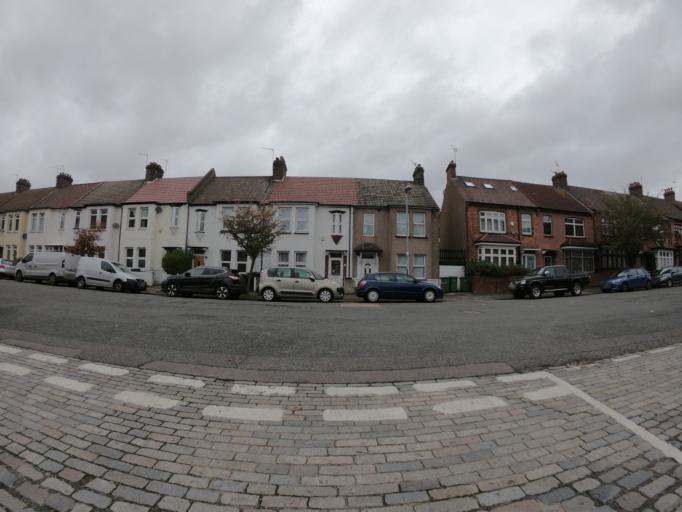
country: GB
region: England
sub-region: Greater London
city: Blackheath
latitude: 51.4813
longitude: 0.0246
